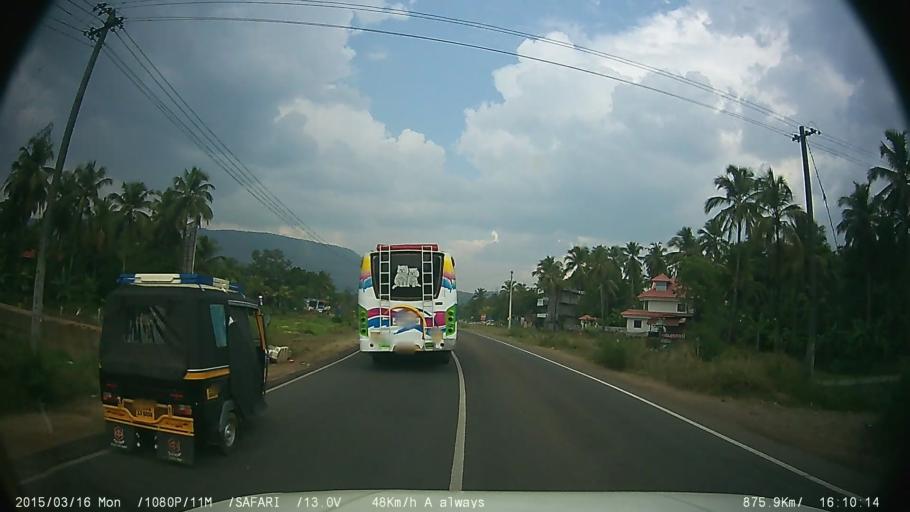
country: IN
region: Kerala
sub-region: Thrissur District
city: Trichur
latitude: 10.5507
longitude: 76.3083
